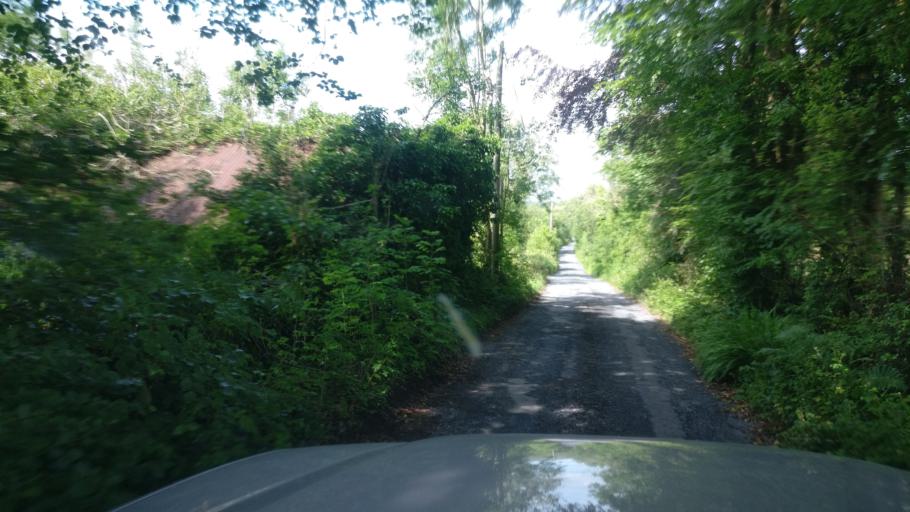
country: IE
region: Connaught
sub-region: County Galway
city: Gort
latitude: 53.0948
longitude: -8.6994
